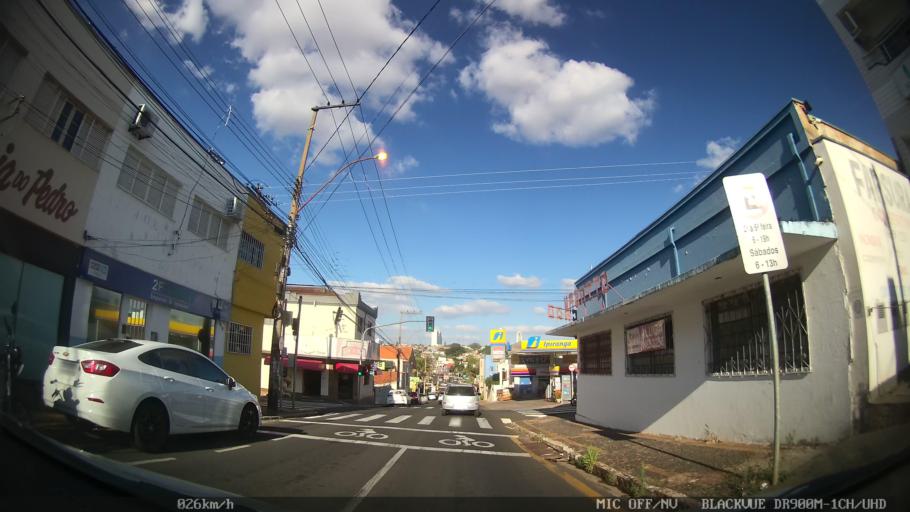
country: BR
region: Sao Paulo
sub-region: Santa Barbara D'Oeste
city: Santa Barbara d'Oeste
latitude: -22.7557
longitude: -47.4094
